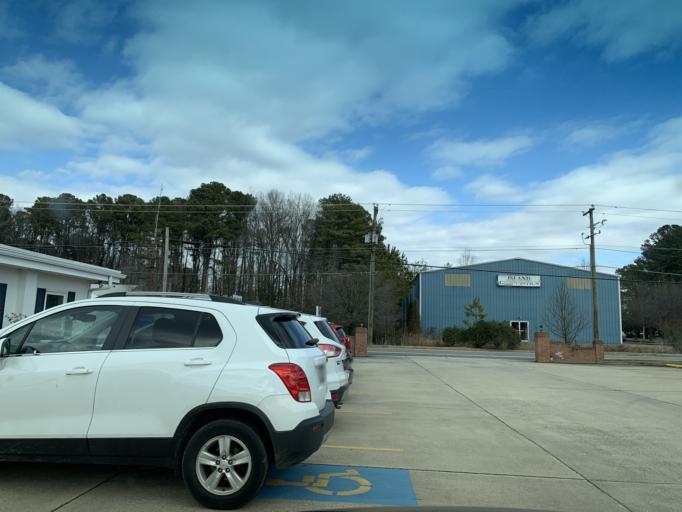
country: US
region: Maryland
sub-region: Queen Anne's County
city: Grasonville
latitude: 38.9632
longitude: -76.2058
